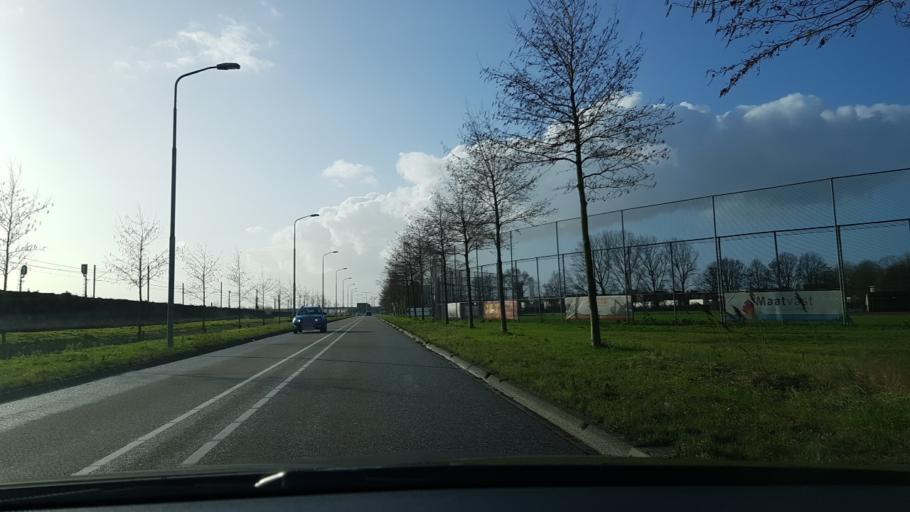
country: NL
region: South Holland
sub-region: Gemeente Kaag en Braassem
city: Oude Wetering
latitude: 52.2569
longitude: 4.6417
